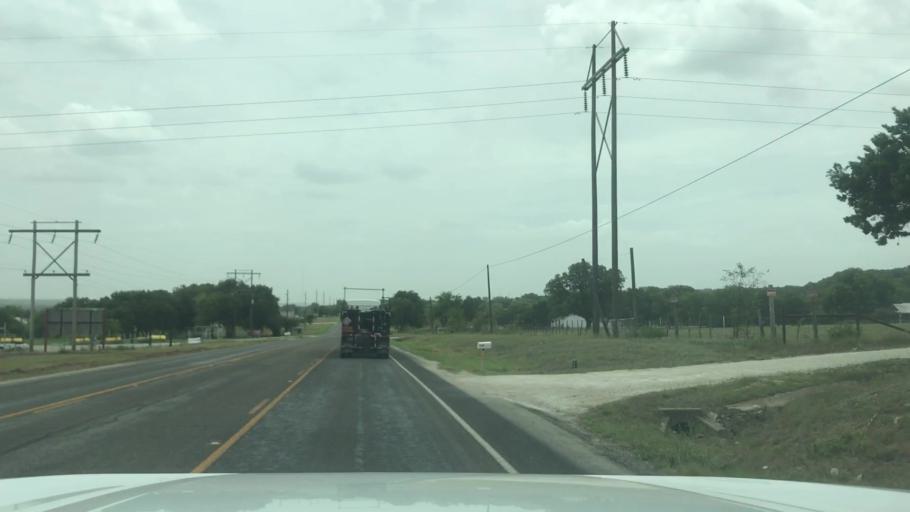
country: US
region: Texas
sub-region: Bosque County
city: Clifton
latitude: 31.7666
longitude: -97.5674
